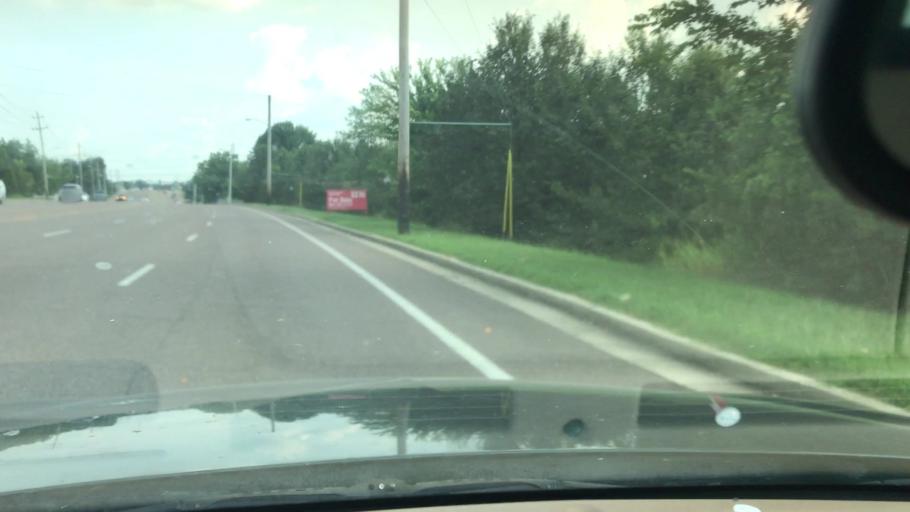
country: US
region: Tennessee
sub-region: Shelby County
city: Bartlett
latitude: 35.1918
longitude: -89.8150
